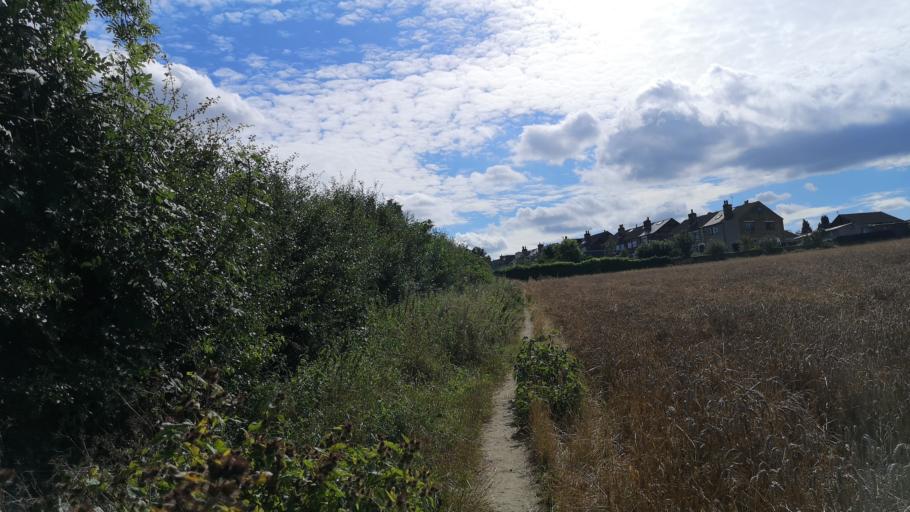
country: GB
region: England
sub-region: City and Borough of Wakefield
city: Low Ackworth
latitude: 53.6472
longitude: -1.3452
